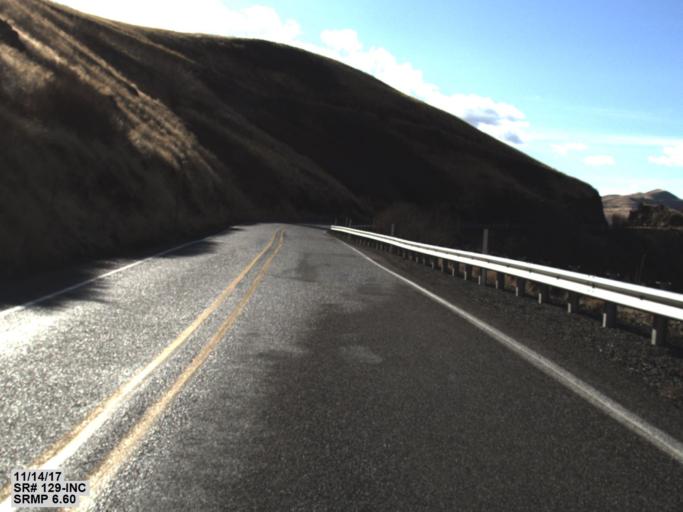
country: US
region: Washington
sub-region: Asotin County
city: Asotin
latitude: 46.0492
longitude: -117.2372
